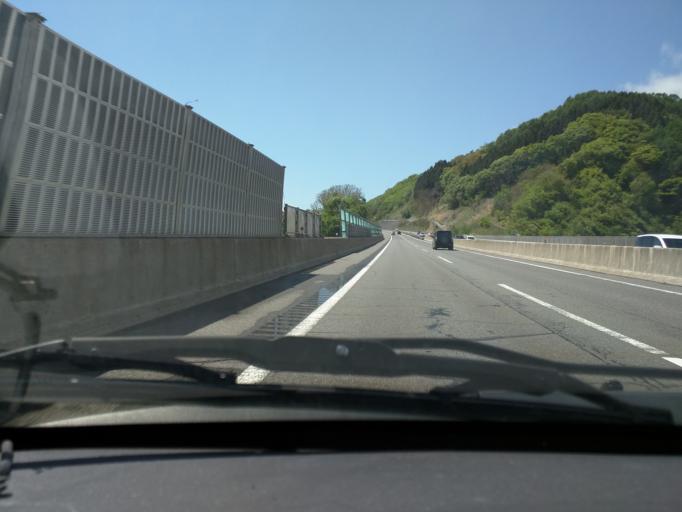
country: JP
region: Nagano
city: Nakano
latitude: 36.7686
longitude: 138.3172
